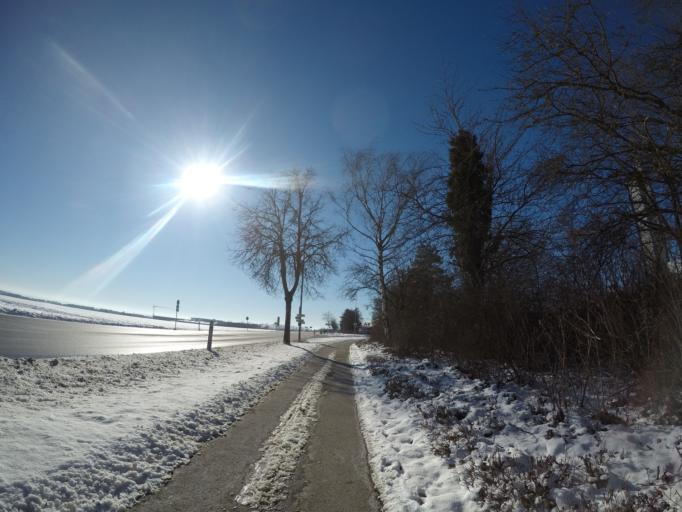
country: DE
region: Baden-Wuerttemberg
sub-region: Tuebingen Region
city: Ulm
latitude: 48.4335
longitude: 9.9857
